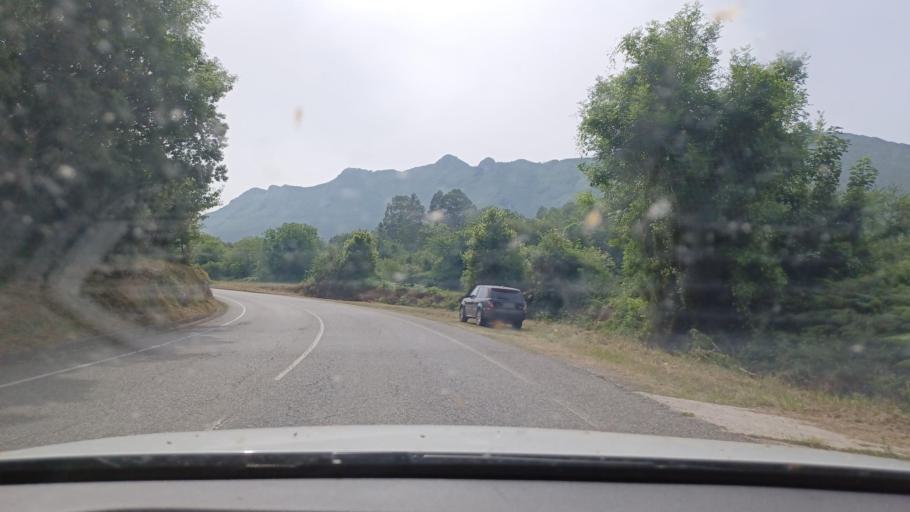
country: ES
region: Asturias
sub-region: Province of Asturias
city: Ribadesella
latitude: 43.4417
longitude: -4.9960
